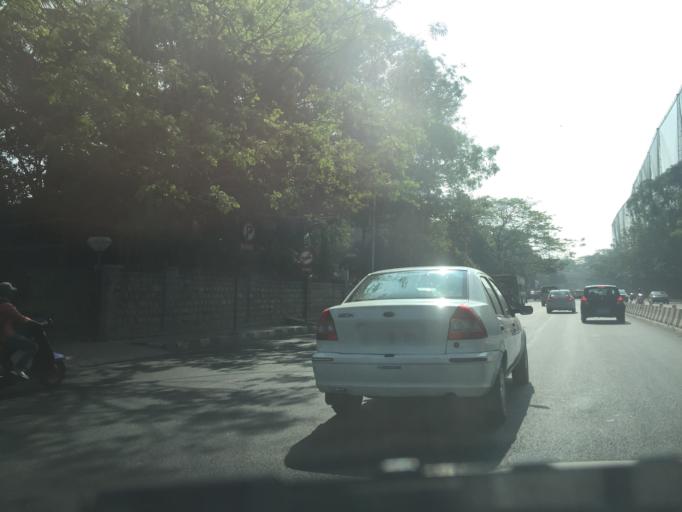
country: IN
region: Karnataka
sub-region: Bangalore Urban
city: Bangalore
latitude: 12.9888
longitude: 77.5863
